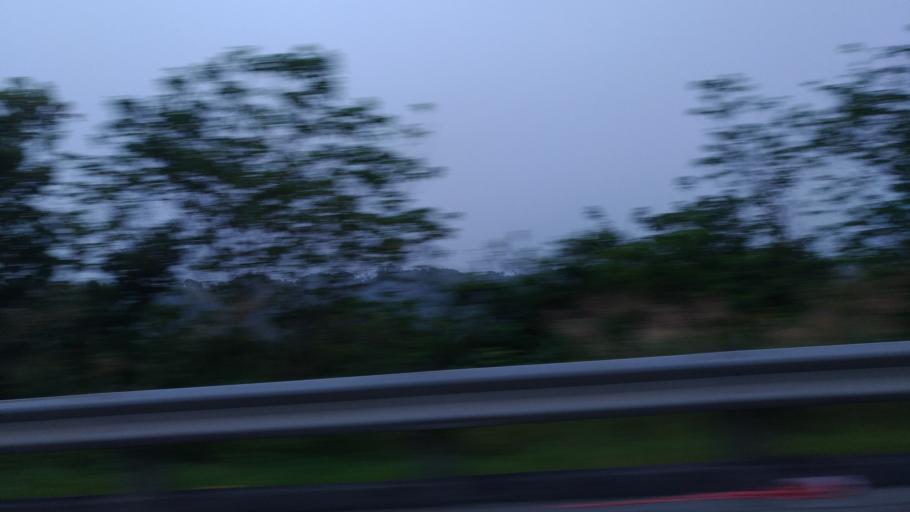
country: TW
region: Taiwan
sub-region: Hsinchu
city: Hsinchu
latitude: 24.7531
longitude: 120.9402
